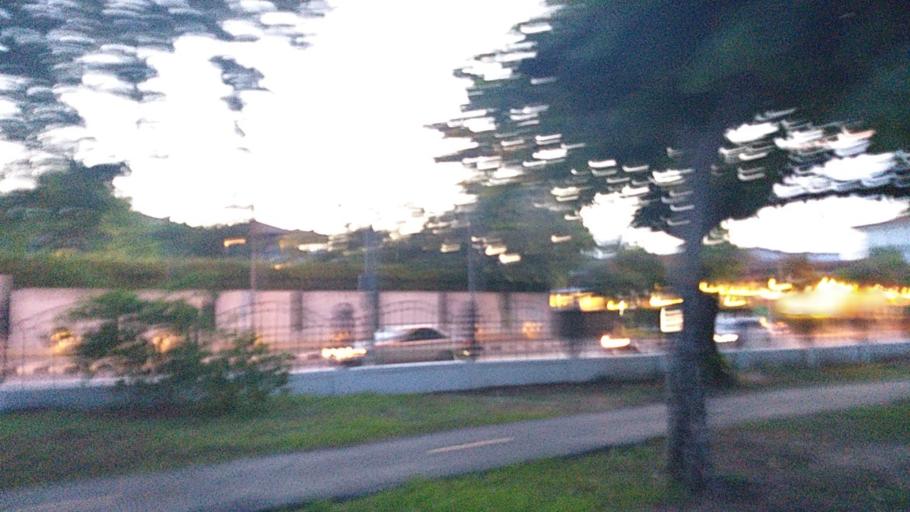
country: TH
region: Khon Kaen
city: Khon Kaen
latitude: 16.4151
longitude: 102.8354
